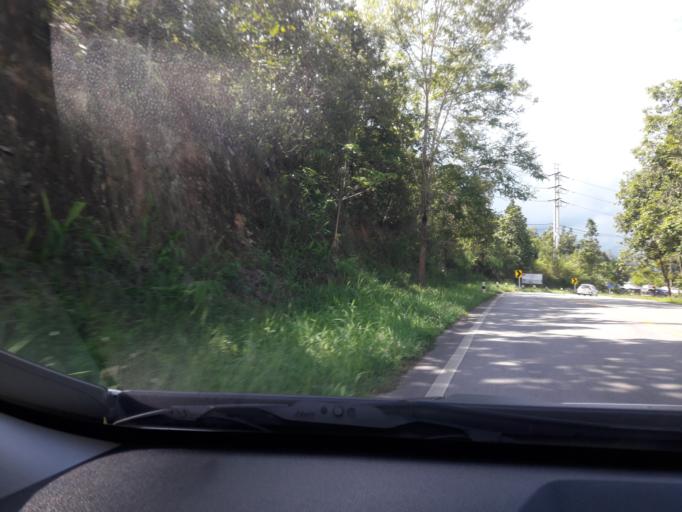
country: TH
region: Mae Hong Son
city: Mae Hi
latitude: 19.3055
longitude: 98.4537
